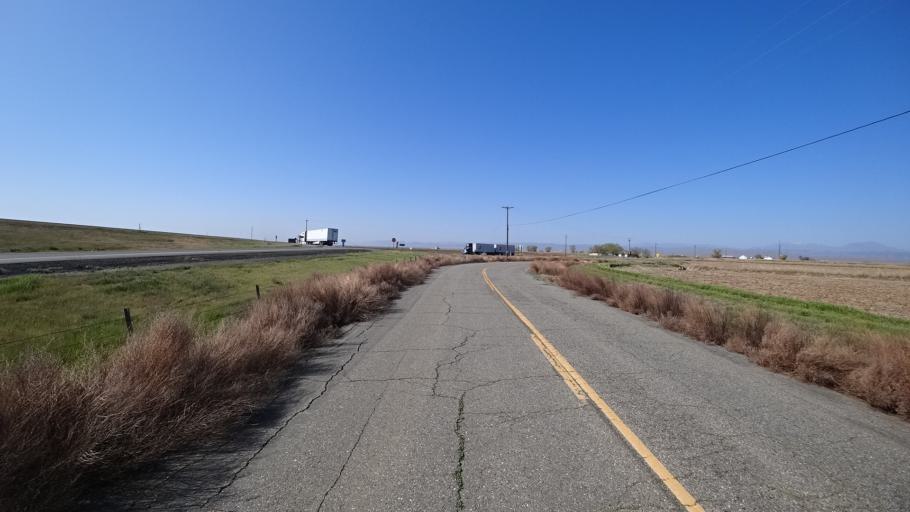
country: US
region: California
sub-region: Glenn County
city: Willows
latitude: 39.4079
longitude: -122.1976
